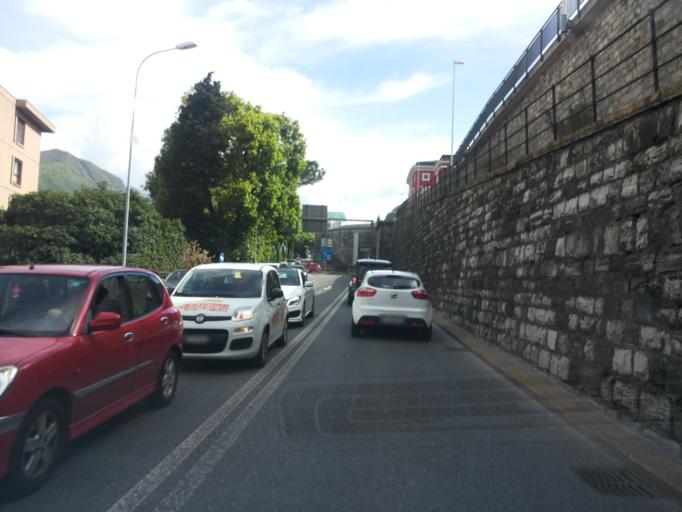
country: CH
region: Ticino
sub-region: Lugano District
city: Massagno
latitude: 46.0067
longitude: 8.9467
